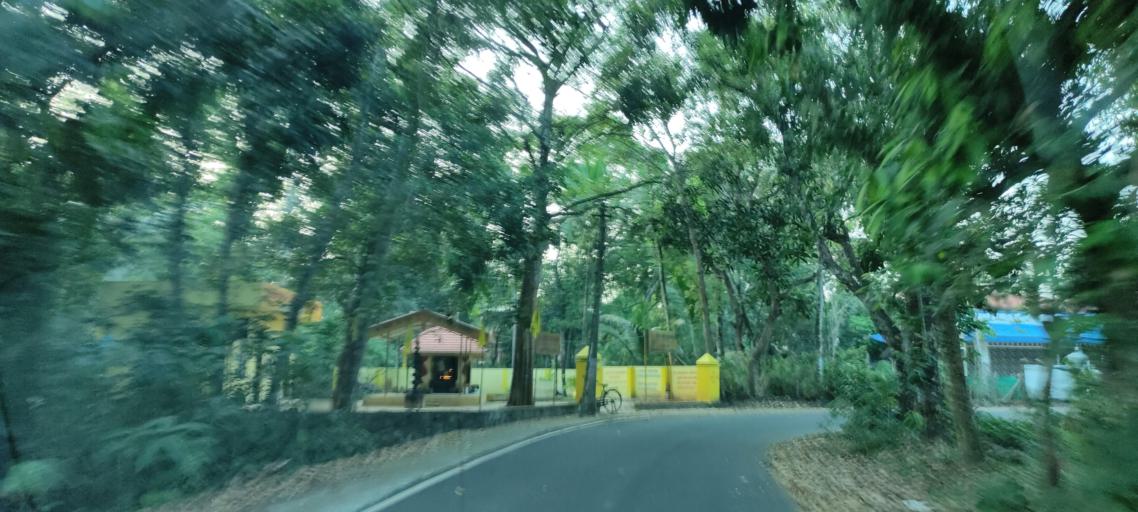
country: IN
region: Kerala
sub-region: Alappuzha
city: Mavelikara
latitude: 9.2782
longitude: 76.5547
